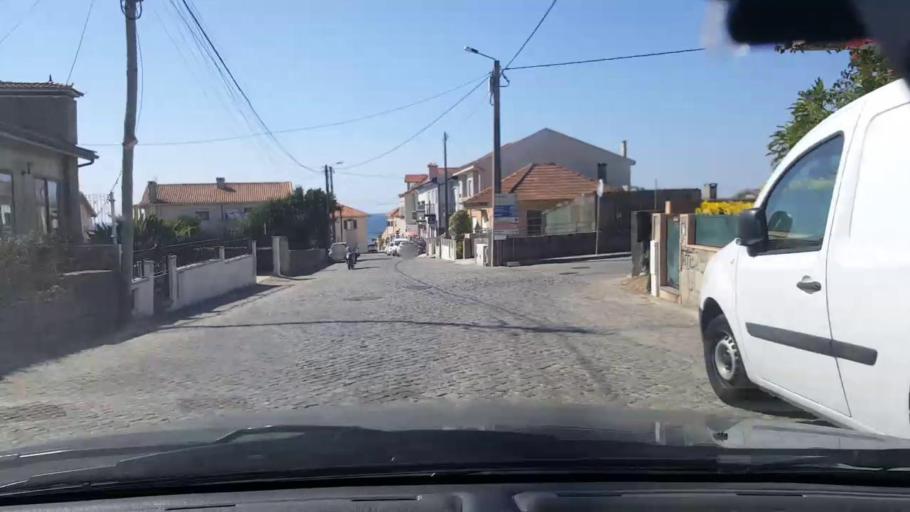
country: PT
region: Porto
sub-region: Matosinhos
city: Lavra
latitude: 41.2916
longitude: -8.7317
